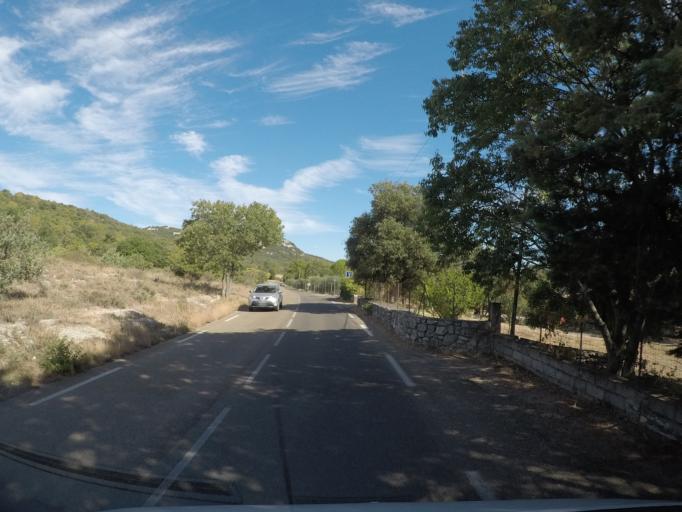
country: FR
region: Languedoc-Roussillon
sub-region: Departement du Gard
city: Saint-Hippolyte-du-Fort
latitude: 43.9609
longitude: 3.8836
